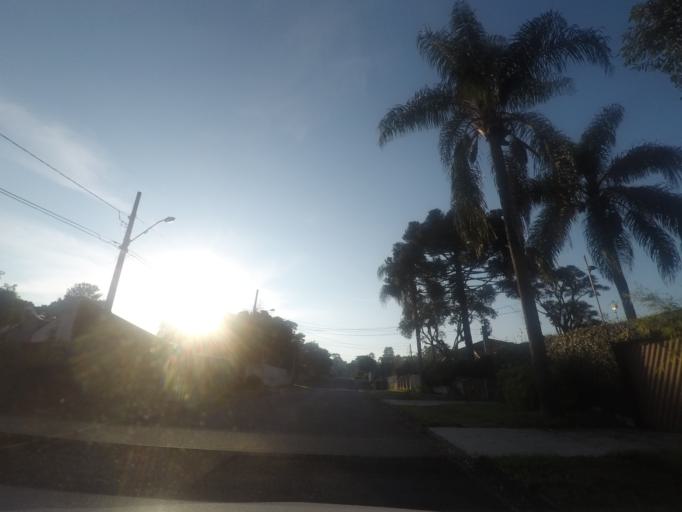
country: BR
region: Parana
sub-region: Curitiba
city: Curitiba
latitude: -25.3961
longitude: -49.2601
